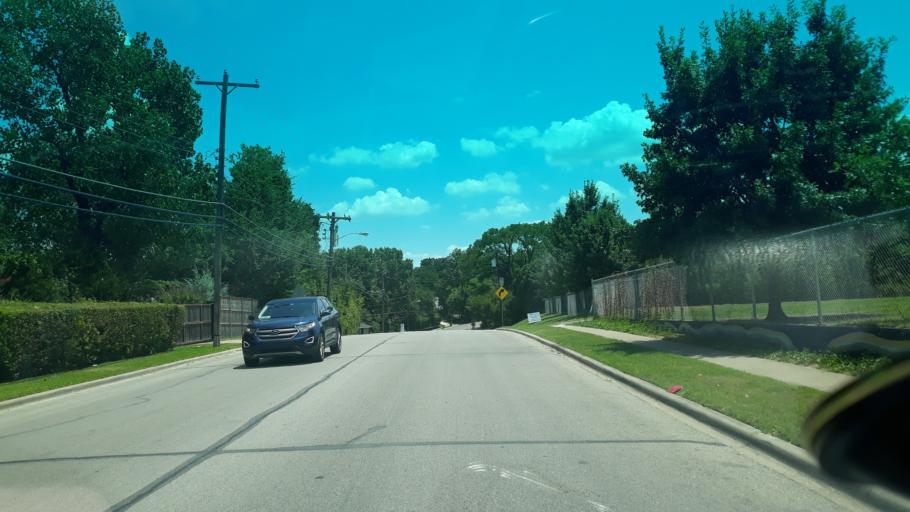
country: US
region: Texas
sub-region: Dallas County
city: Highland Park
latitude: 32.8261
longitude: -96.7427
